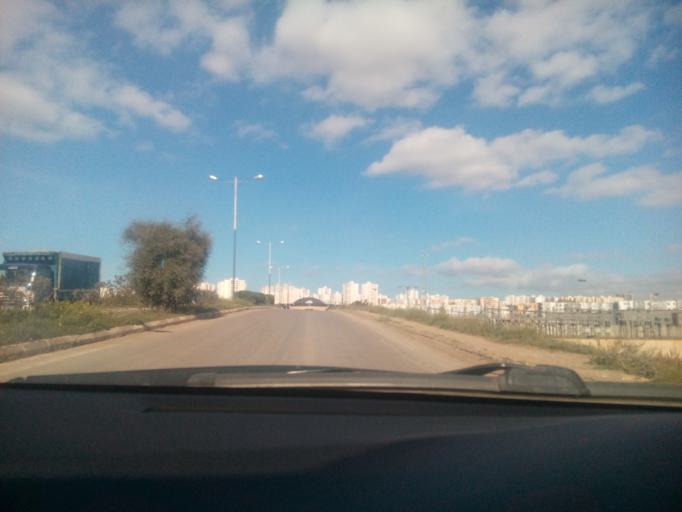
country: DZ
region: Oran
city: Bir el Djir
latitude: 35.6909
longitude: -0.5754
